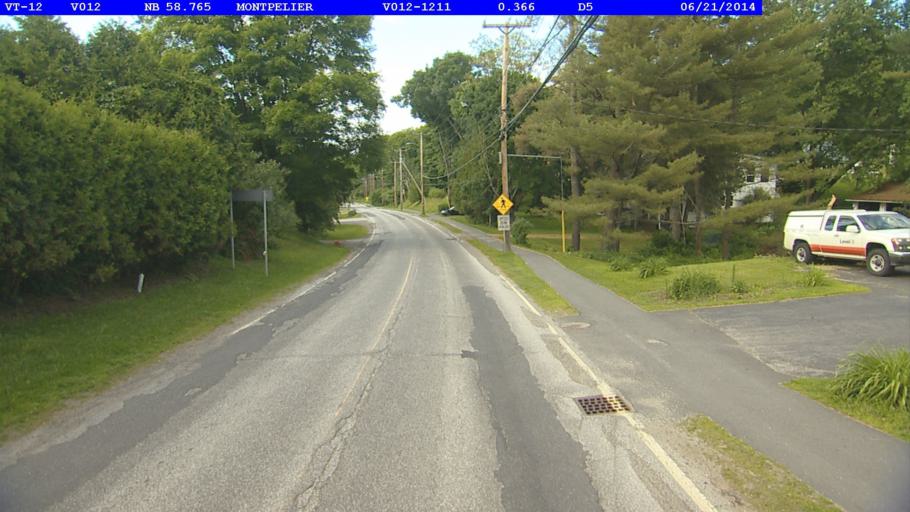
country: US
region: Vermont
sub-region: Washington County
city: Montpelier
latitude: 44.2496
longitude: -72.5824
